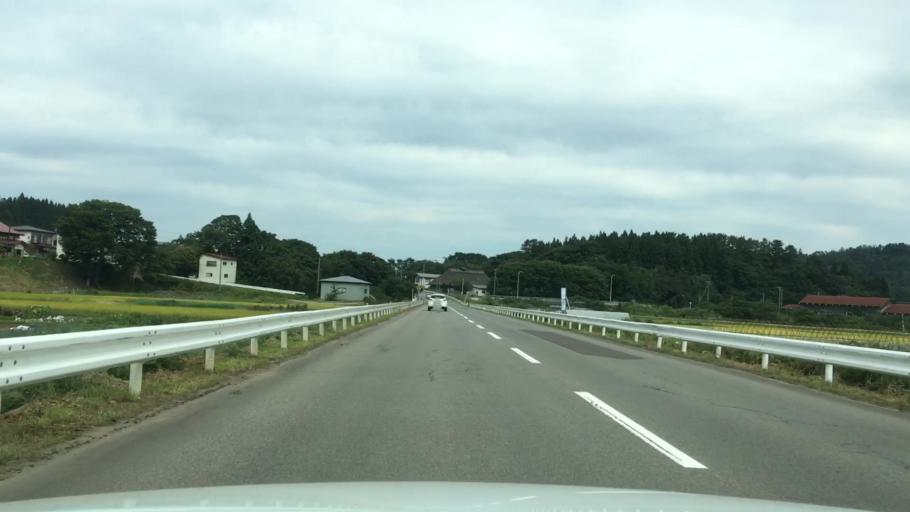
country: JP
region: Aomori
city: Shimokizukuri
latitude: 40.7548
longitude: 140.2308
